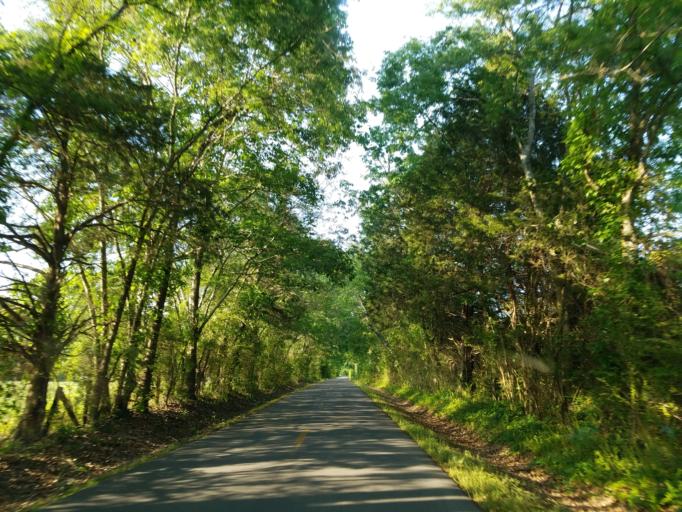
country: US
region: Georgia
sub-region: Gordon County
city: Calhoun
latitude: 34.5318
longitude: -85.1103
